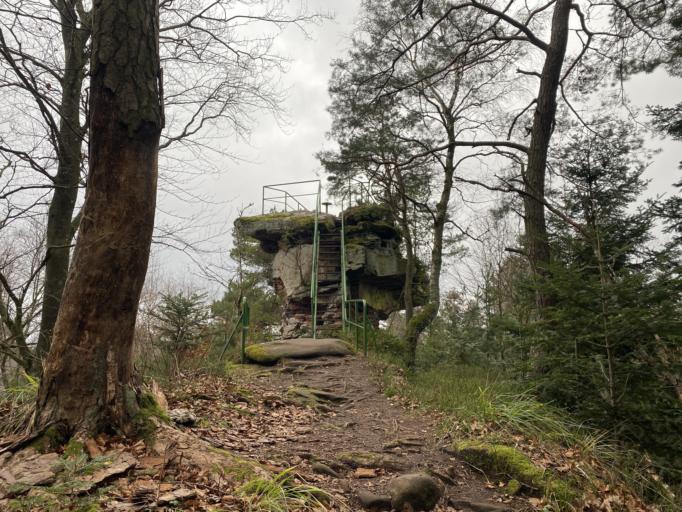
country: DE
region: Rheinland-Pfalz
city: Busenberg
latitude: 49.1123
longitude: 7.8220
